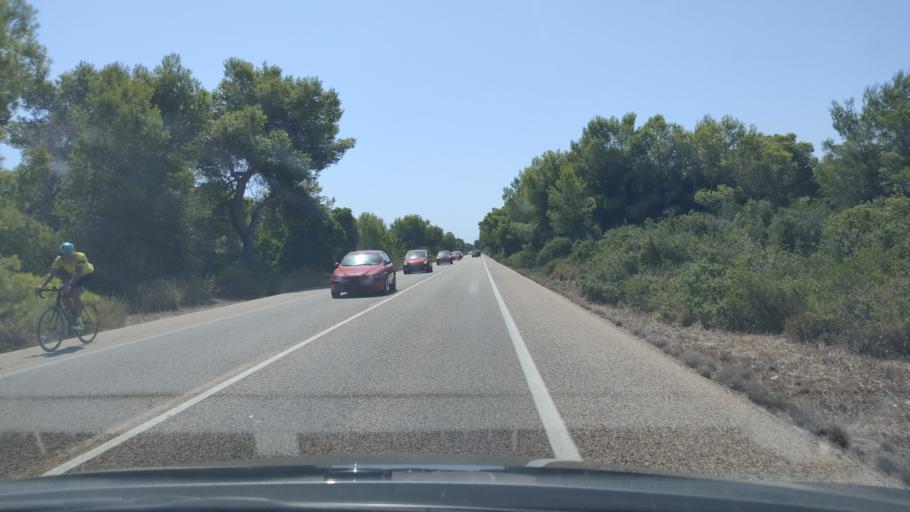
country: ES
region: Valencia
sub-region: Provincia de Valencia
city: Sollana
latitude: 39.3369
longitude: -0.3168
